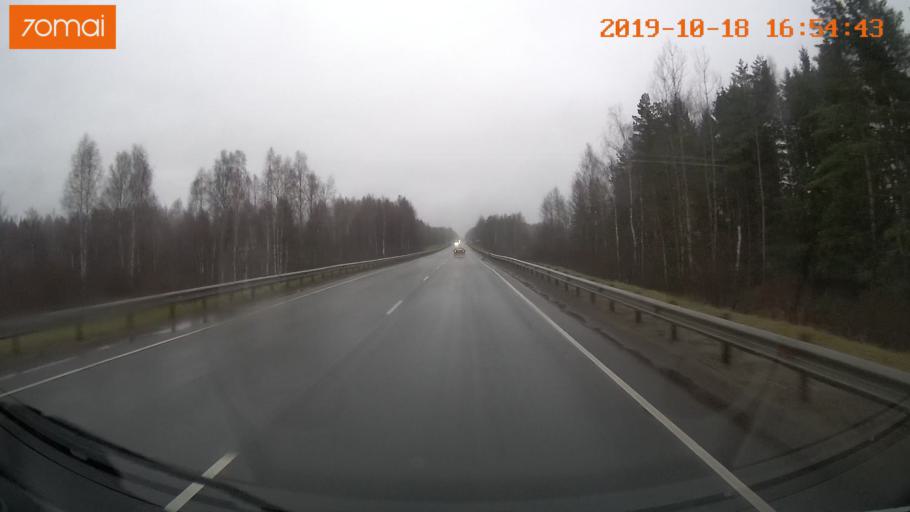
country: RU
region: Ivanovo
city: Novoye Leushino
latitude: 56.6340
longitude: 40.5735
